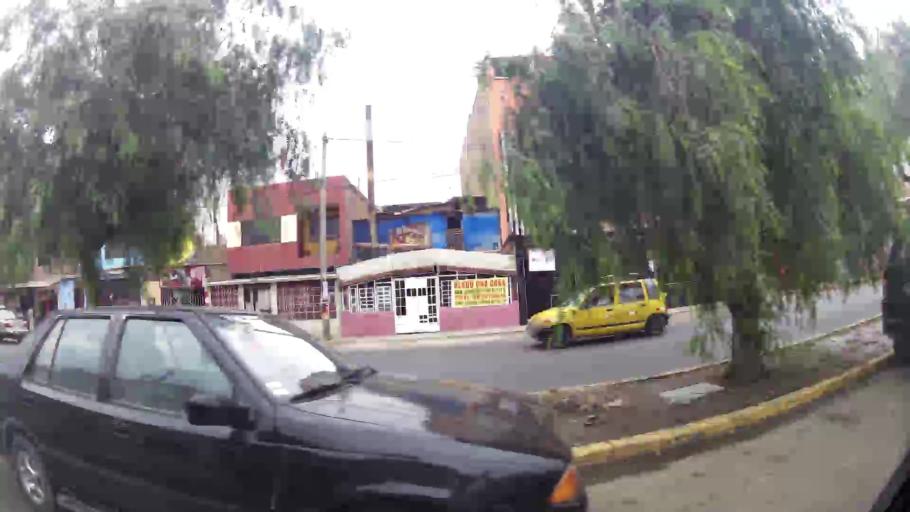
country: PE
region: La Libertad
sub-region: Provincia de Trujillo
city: Trujillo
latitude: -8.1182
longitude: -79.0279
